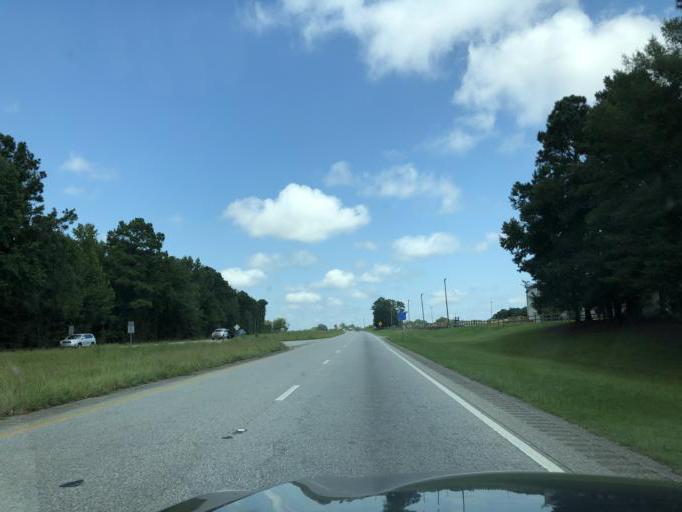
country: US
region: Alabama
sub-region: Henry County
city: Abbeville
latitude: 31.5912
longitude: -85.2779
